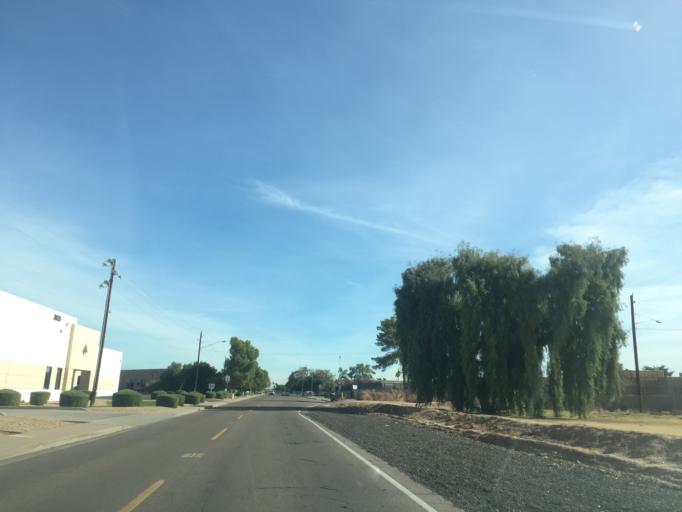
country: US
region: Arizona
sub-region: Maricopa County
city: Guadalupe
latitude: 33.3997
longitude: -112.0035
